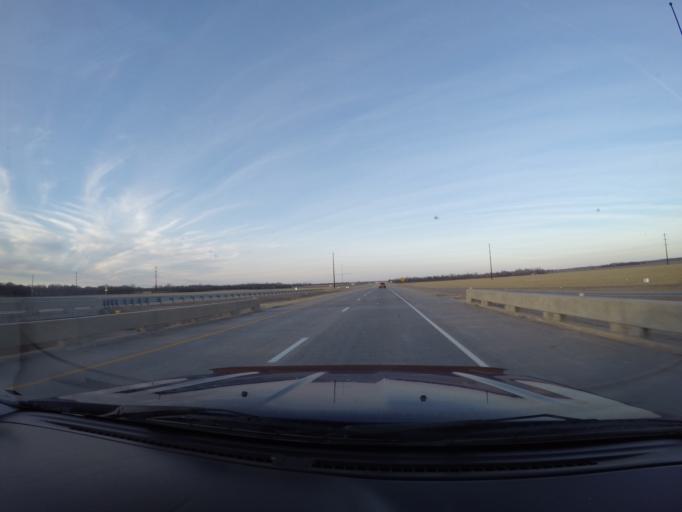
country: US
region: Kansas
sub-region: Saline County
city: Salina
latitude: 38.7400
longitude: -97.6180
